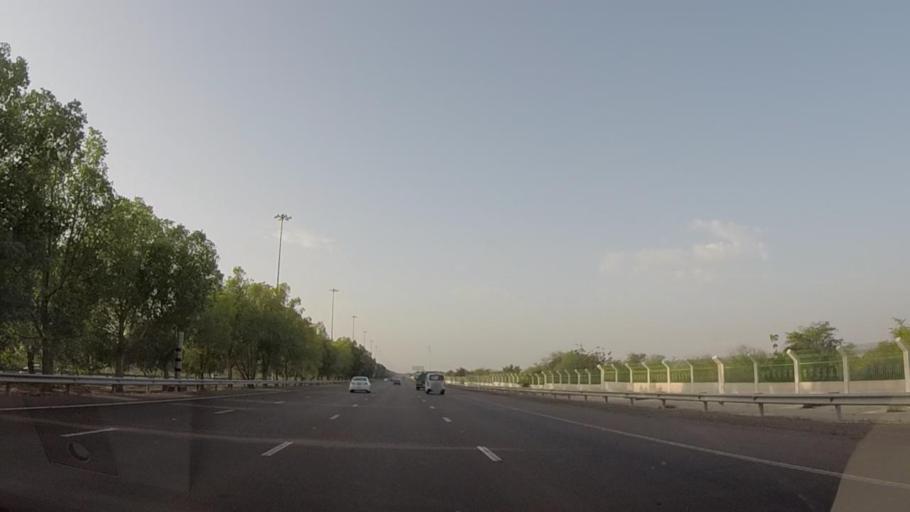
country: AE
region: Dubai
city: Dubai
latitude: 24.7888
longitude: 54.8582
